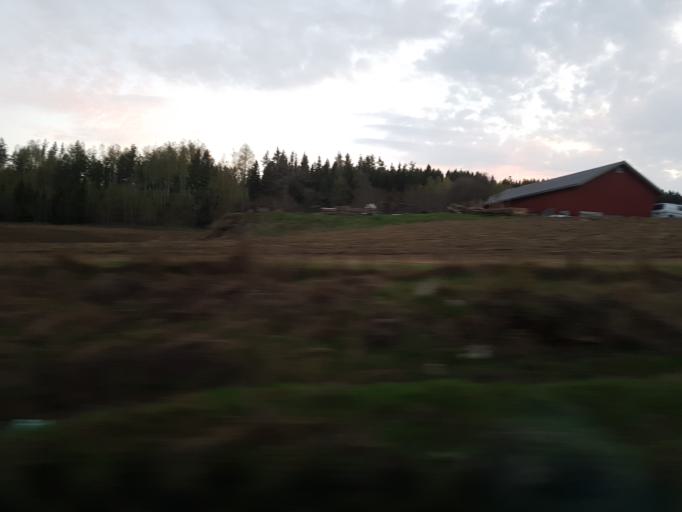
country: NO
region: Hedmark
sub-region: Ringsaker
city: Moelv
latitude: 60.9178
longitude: 10.7176
